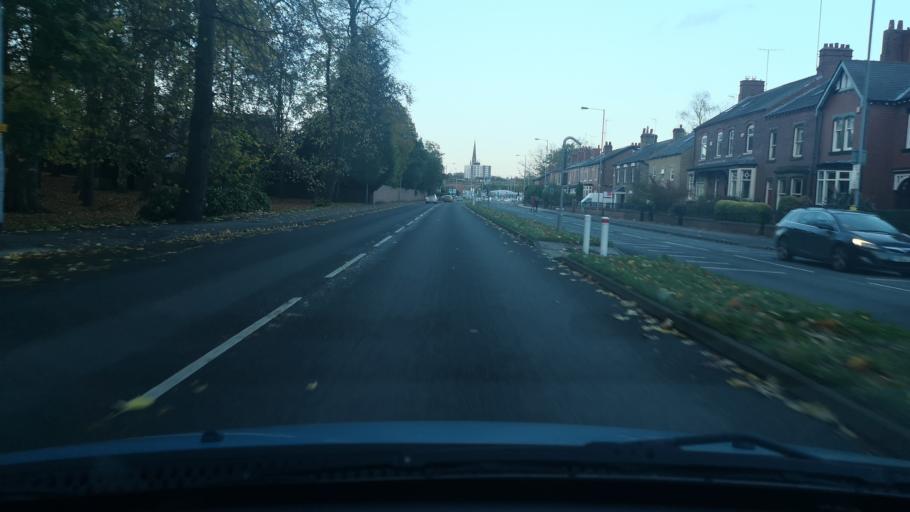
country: GB
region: England
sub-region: City and Borough of Wakefield
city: Wakefield
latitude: 53.6737
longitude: -1.5025
